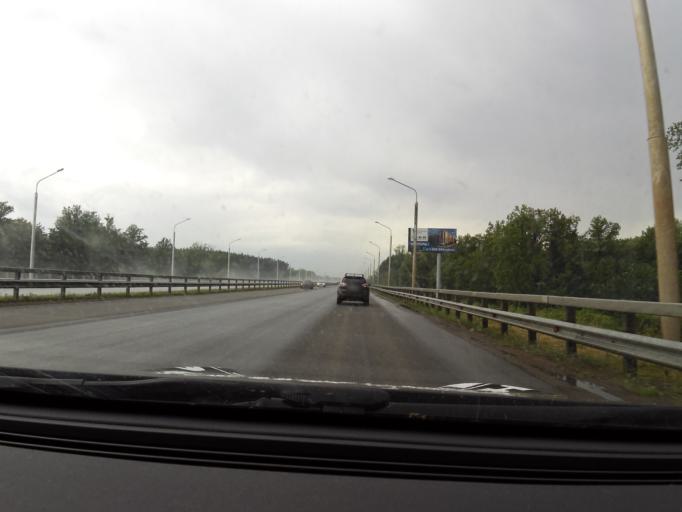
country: RU
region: Bashkortostan
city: Ufa
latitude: 54.7785
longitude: 55.9388
